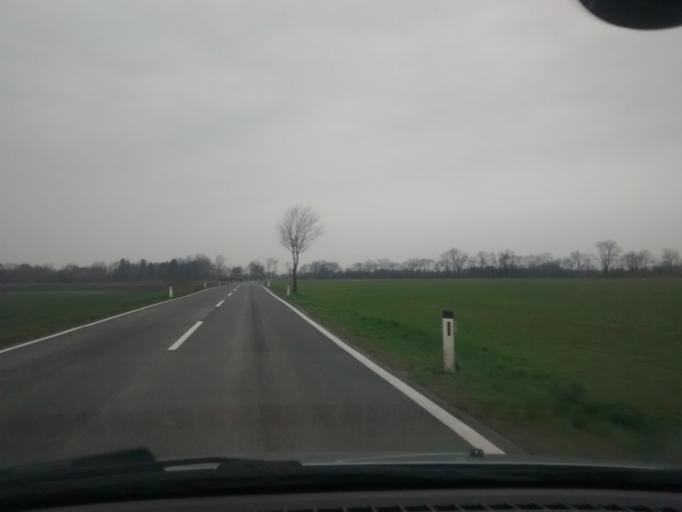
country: AT
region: Lower Austria
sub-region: Politischer Bezirk Wien-Umgebung
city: Moosbrunn
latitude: 48.0054
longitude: 16.4180
